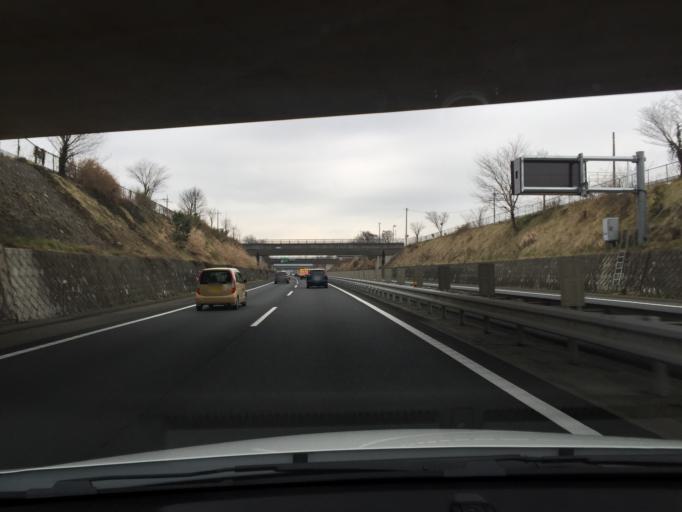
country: JP
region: Saitama
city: Hanno
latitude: 35.8046
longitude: 139.3369
